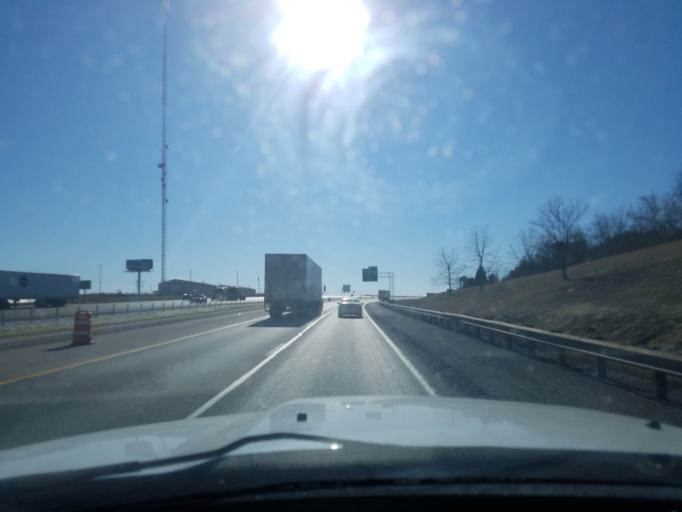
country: US
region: Kentucky
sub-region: Hardin County
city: Elizabethtown
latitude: 37.6848
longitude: -85.8430
